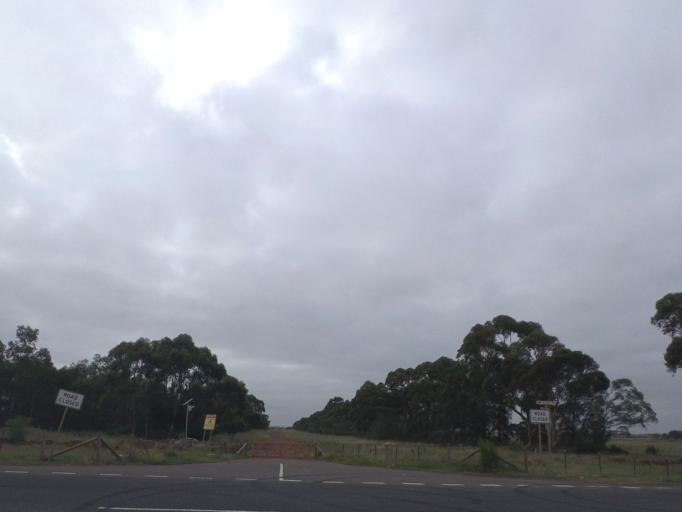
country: AU
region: Victoria
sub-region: Melton
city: Rockbank
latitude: -37.7087
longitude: 144.6563
